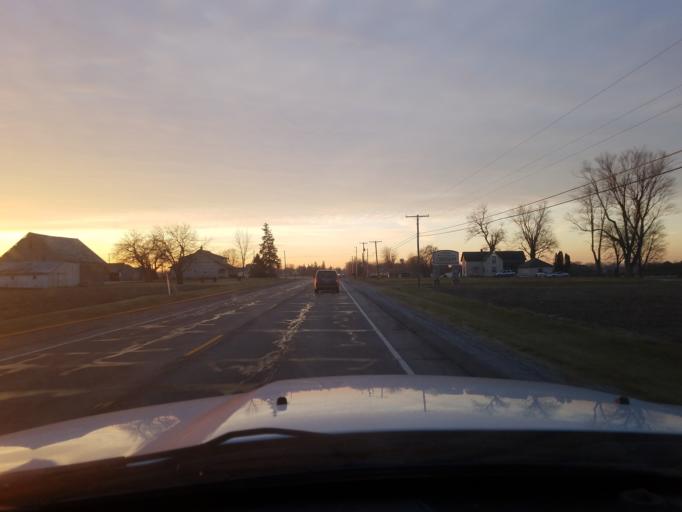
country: US
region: Indiana
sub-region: Wells County
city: Ossian
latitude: 40.8974
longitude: -85.1667
